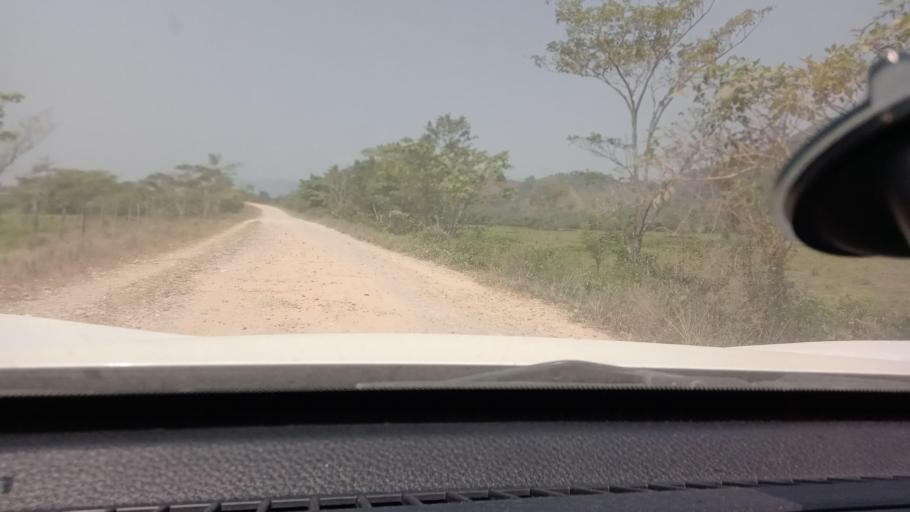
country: MX
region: Tabasco
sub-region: Huimanguillo
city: Francisco Rueda
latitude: 17.5141
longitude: -93.8952
